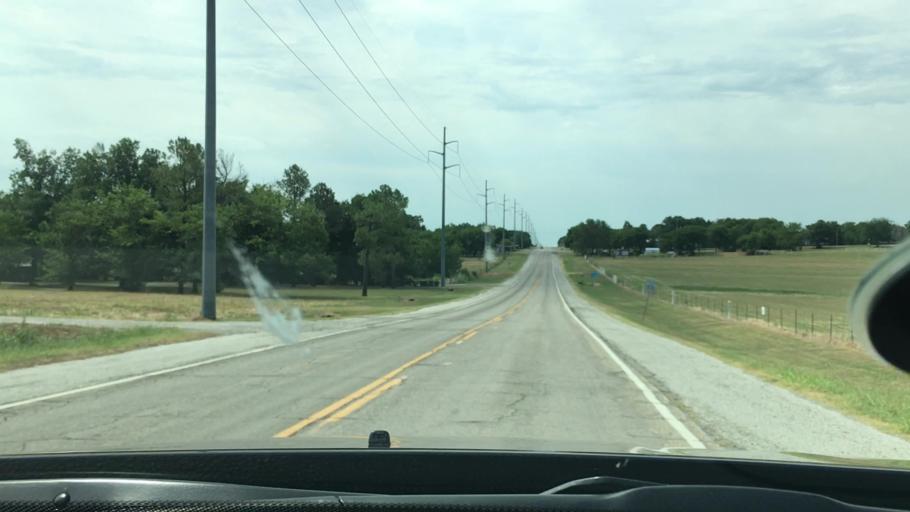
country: US
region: Oklahoma
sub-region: Carter County
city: Ardmore
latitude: 34.3196
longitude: -97.1430
